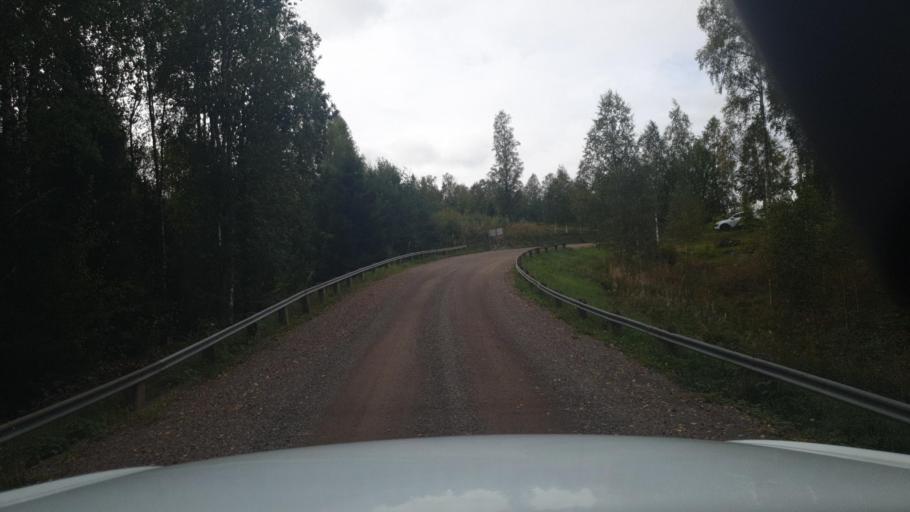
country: SE
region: Vaermland
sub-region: Eda Kommun
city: Charlottenberg
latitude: 60.0891
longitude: 12.5098
